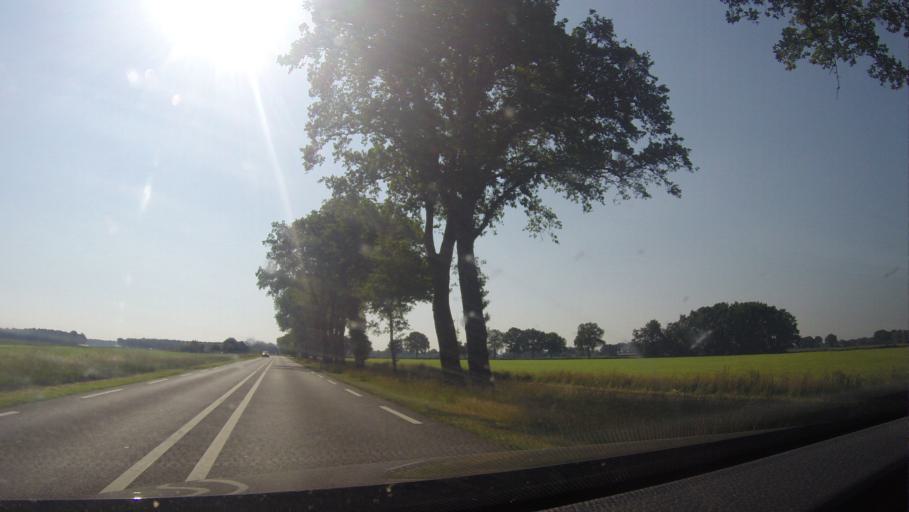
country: NL
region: Overijssel
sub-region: Gemeente Raalte
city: Raalte
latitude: 52.3275
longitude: 6.3141
